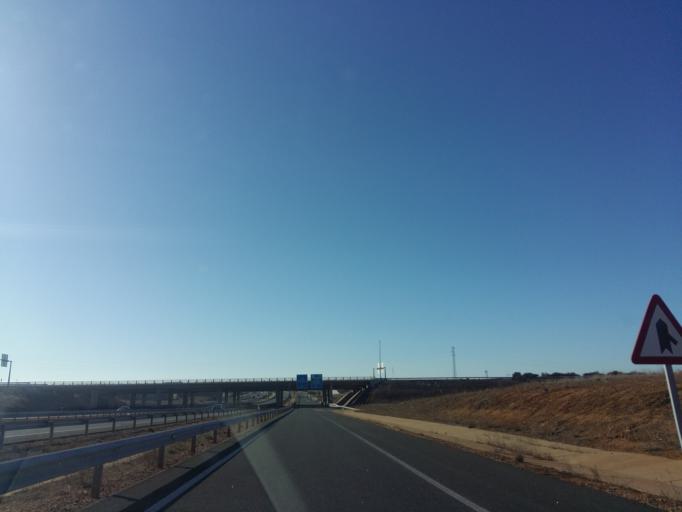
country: ES
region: Castille and Leon
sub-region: Provincia de Palencia
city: Abia de las Torres
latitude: 42.4061
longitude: -4.3888
